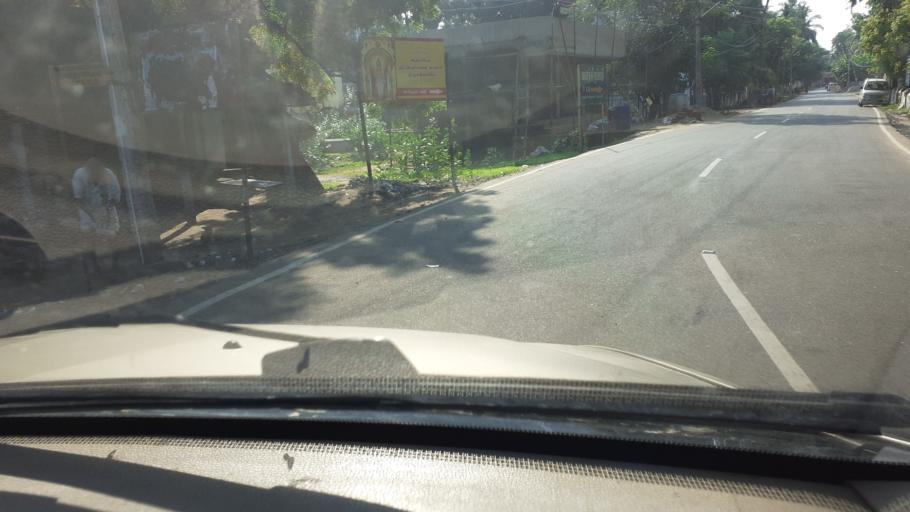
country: IN
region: Tamil Nadu
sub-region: Thoothukkudi
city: Eral
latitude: 8.5791
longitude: 78.0351
